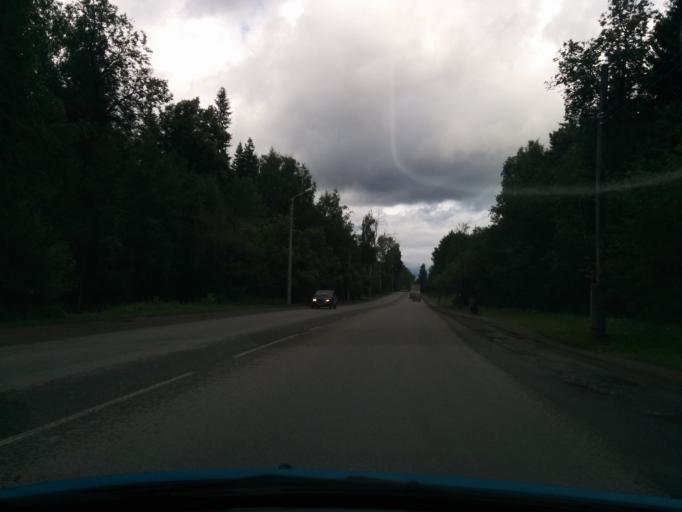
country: RU
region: Perm
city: Kondratovo
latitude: 58.0452
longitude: 56.0707
